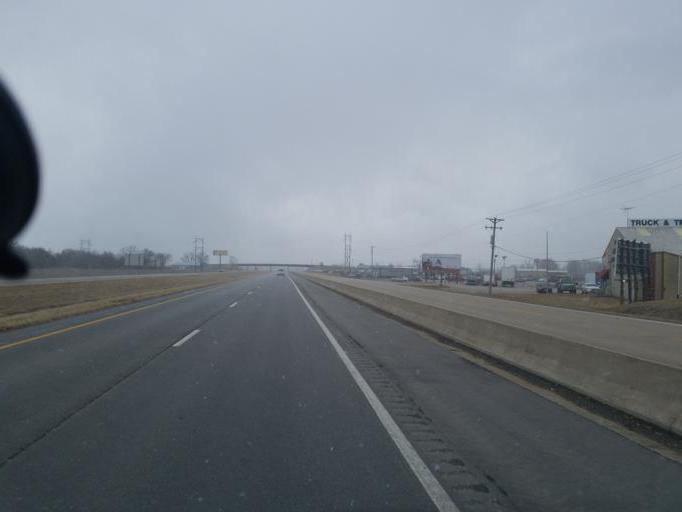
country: US
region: Missouri
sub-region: Randolph County
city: Moberly
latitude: 39.4359
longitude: -92.4191
